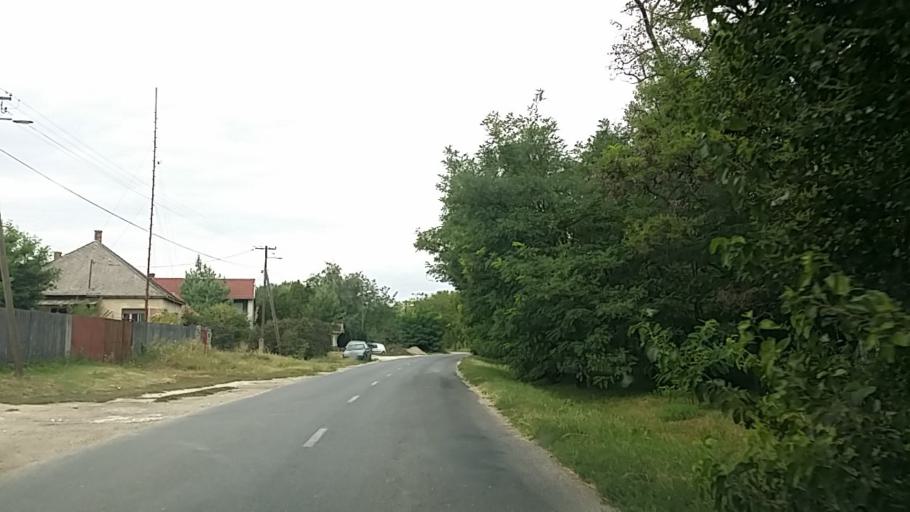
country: HU
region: Komarom-Esztergom
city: Komarom
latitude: 47.7247
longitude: 18.1616
